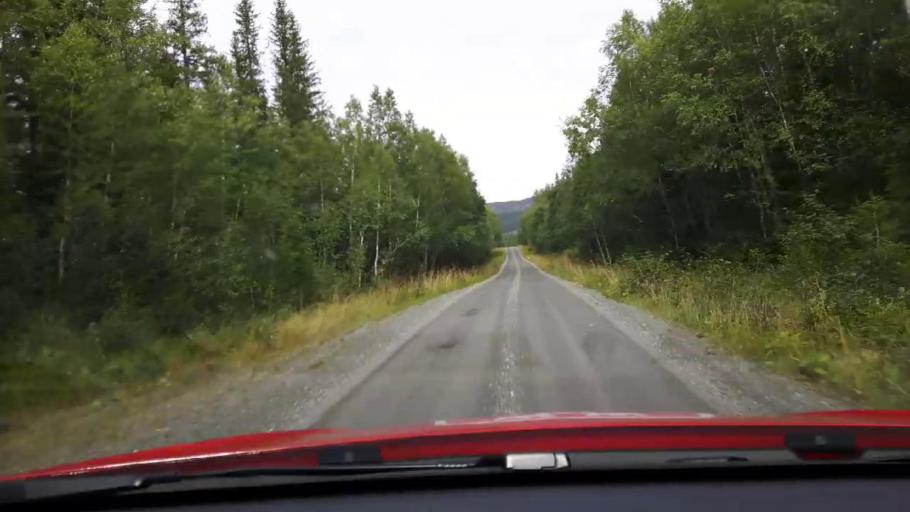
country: SE
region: Jaemtland
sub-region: Are Kommun
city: Are
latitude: 63.7969
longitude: 13.1092
